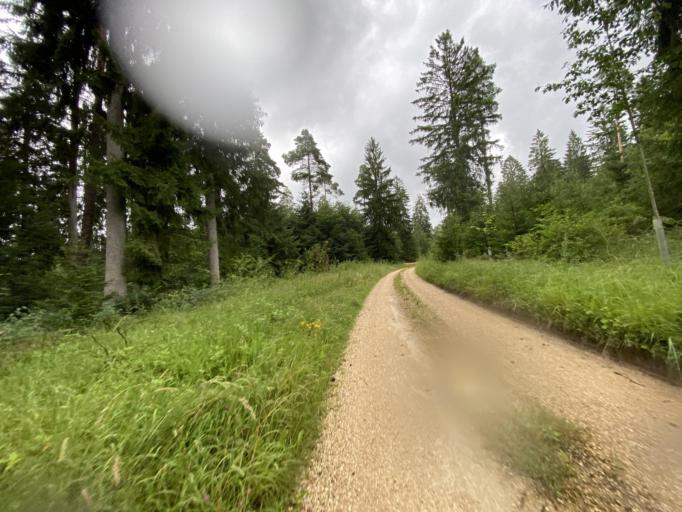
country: DE
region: Baden-Wuerttemberg
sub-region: Tuebingen Region
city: Sigmaringen
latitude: 48.1219
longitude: 9.2255
